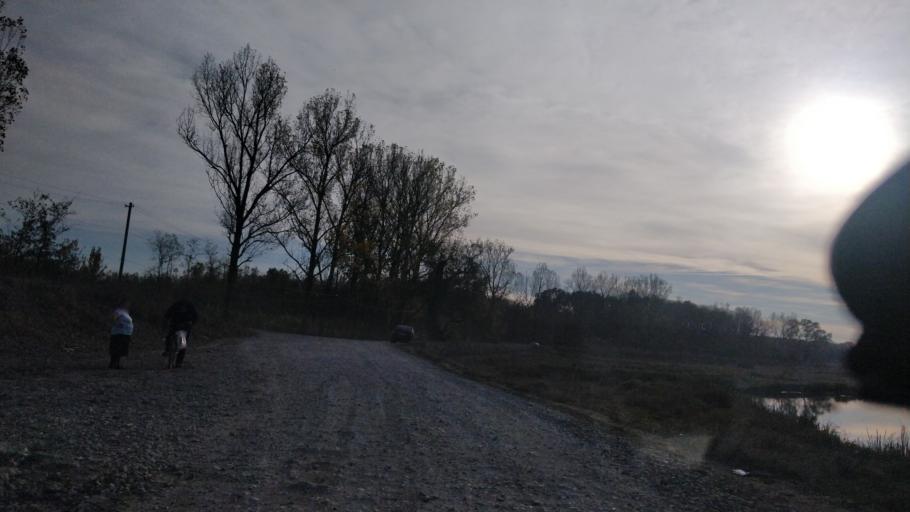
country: RO
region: Giurgiu
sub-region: Comuna Bucsani
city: Bucsani
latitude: 44.3424
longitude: 25.6696
